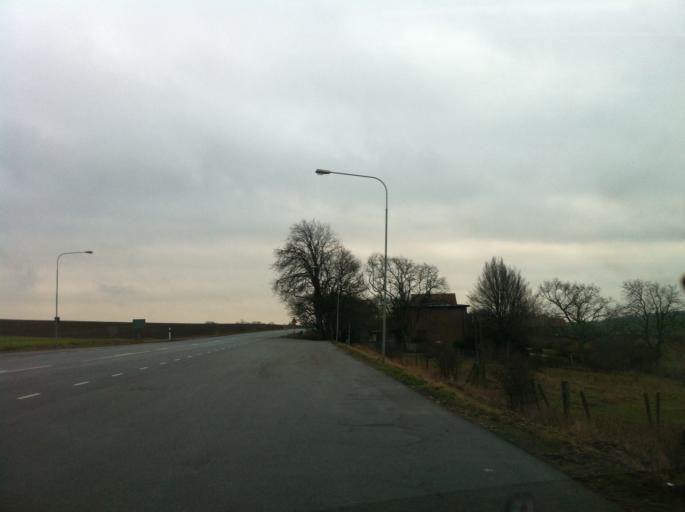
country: SE
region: Skane
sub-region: Helsingborg
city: Glumslov
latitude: 55.9308
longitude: 12.8177
